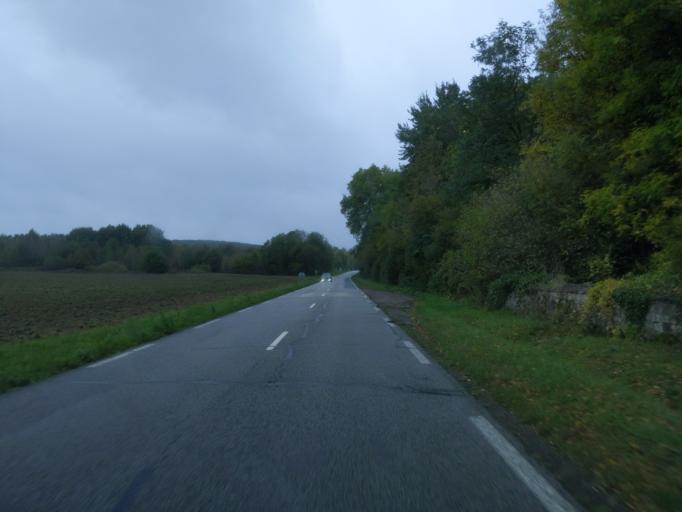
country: FR
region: Ile-de-France
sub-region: Departement des Yvelines
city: Dampierre-en-Yvelines
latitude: 48.6927
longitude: 1.9756
